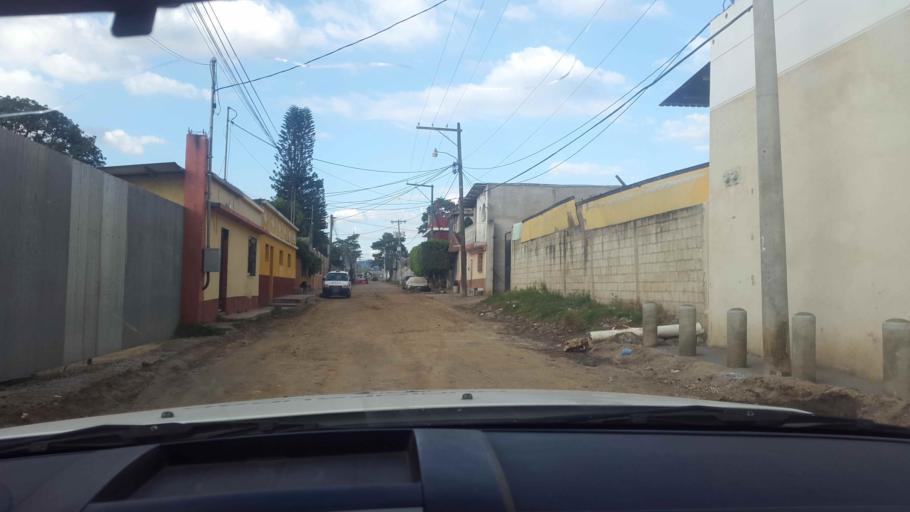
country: GT
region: Guatemala
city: Petapa
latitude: 14.5132
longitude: -90.5430
